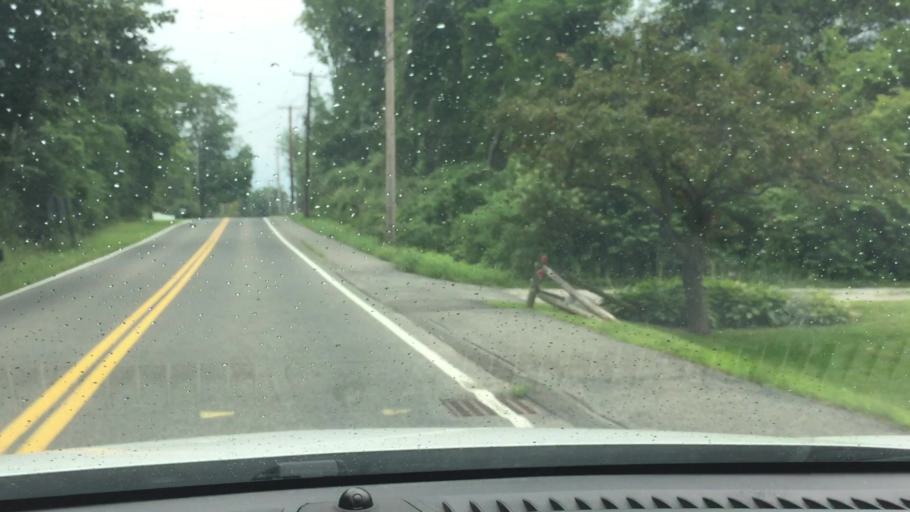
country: US
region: Massachusetts
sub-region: Berkshire County
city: Lenox
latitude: 42.3499
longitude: -73.2565
